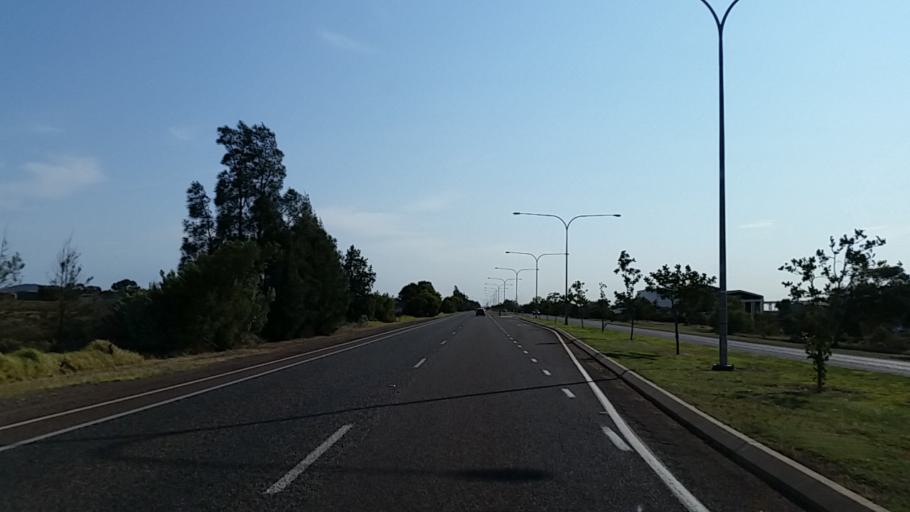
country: AU
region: South Australia
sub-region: Whyalla
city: Whyalla
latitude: -33.0410
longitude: 137.5502
